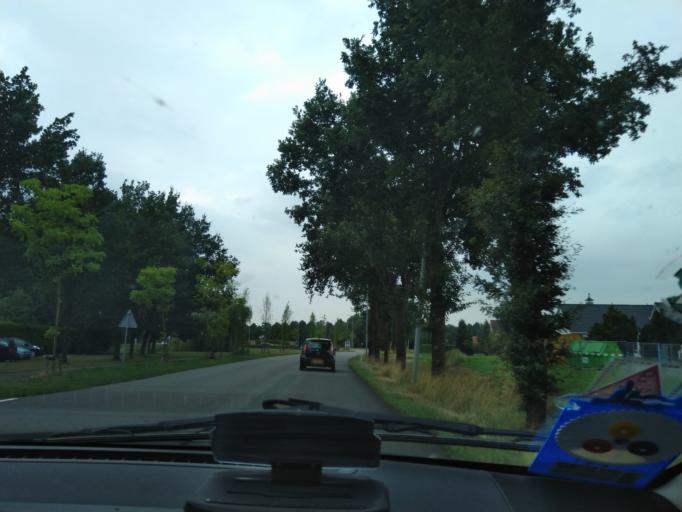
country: NL
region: Groningen
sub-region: Gemeente Pekela
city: Oude Pekela
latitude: 53.1134
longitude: 7.0237
